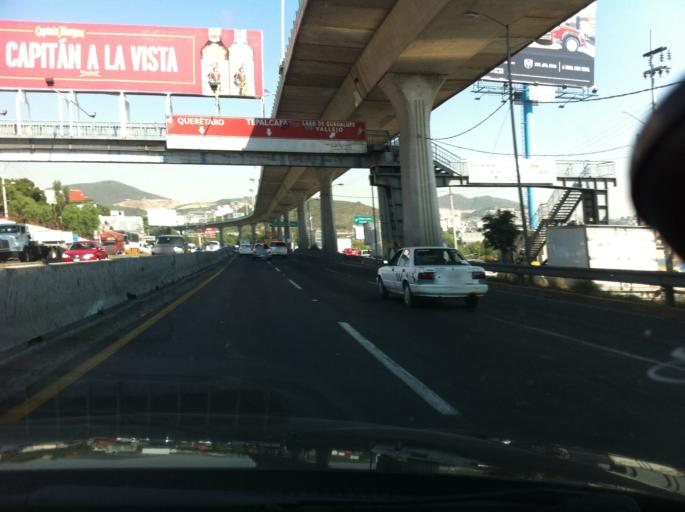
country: MX
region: Mexico
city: Tlalnepantla
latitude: 19.5606
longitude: -99.2063
